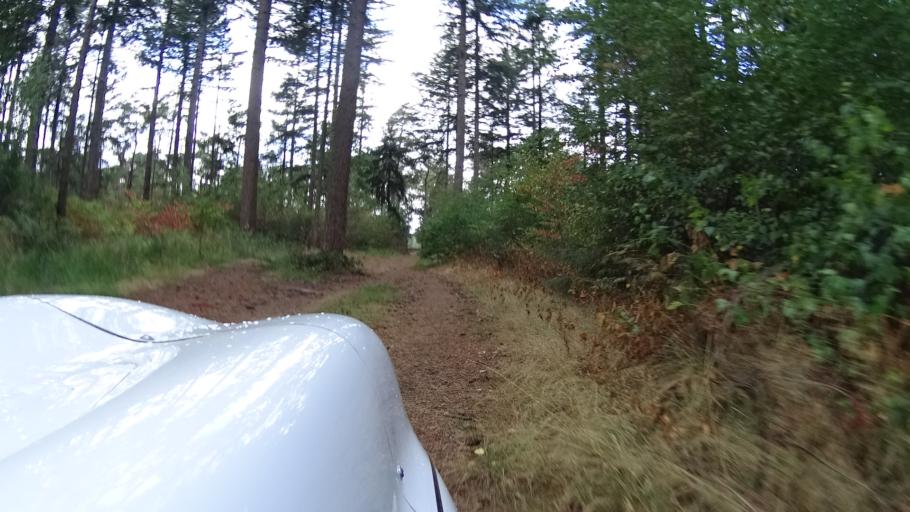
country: NL
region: Utrecht
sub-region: Gemeente Soest
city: Soest
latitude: 52.1855
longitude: 5.2535
